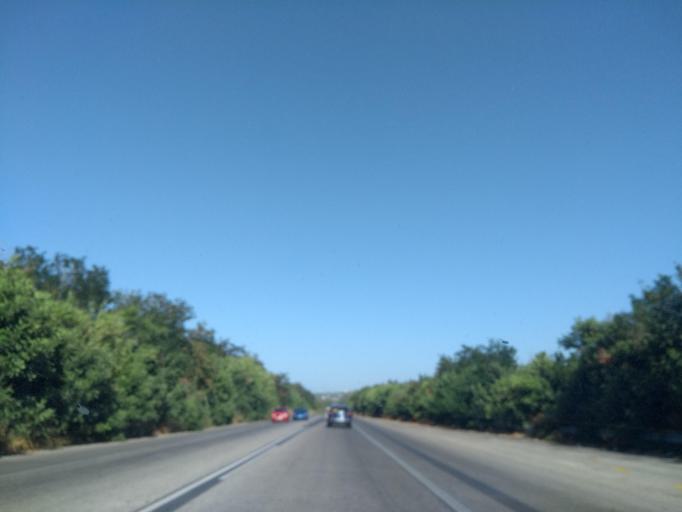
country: GR
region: Crete
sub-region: Nomos Chanias
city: Gerani
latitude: 35.5157
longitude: 23.8664
